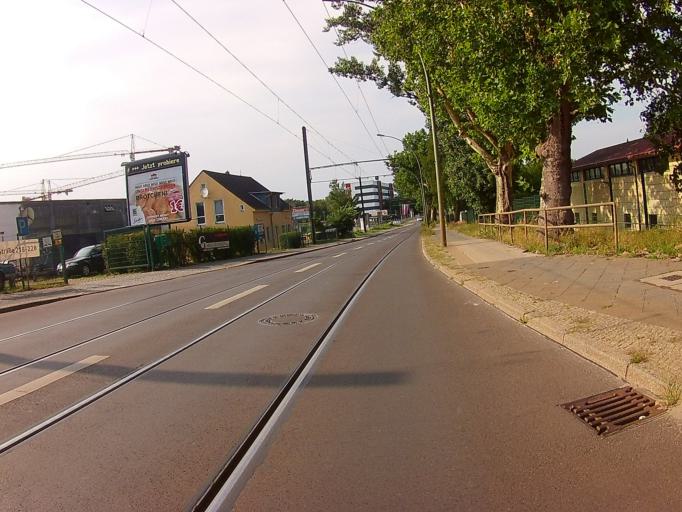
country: DE
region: Berlin
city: Grunau
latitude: 52.4286
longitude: 13.5725
